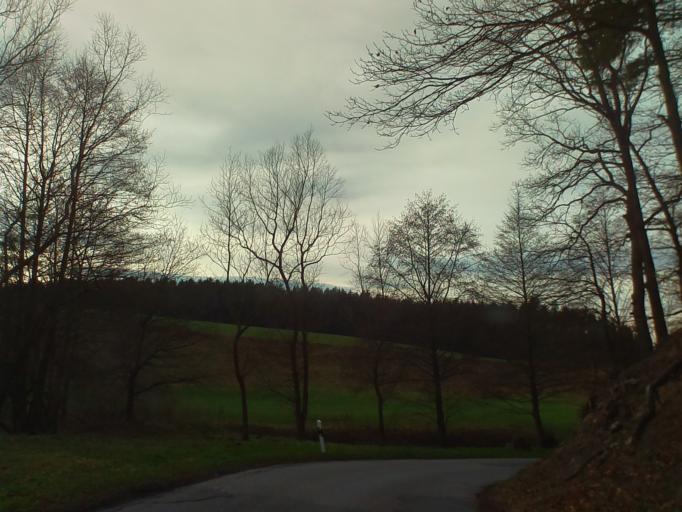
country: DE
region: Thuringia
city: Unterbodnitz
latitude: 50.8213
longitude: 11.6385
